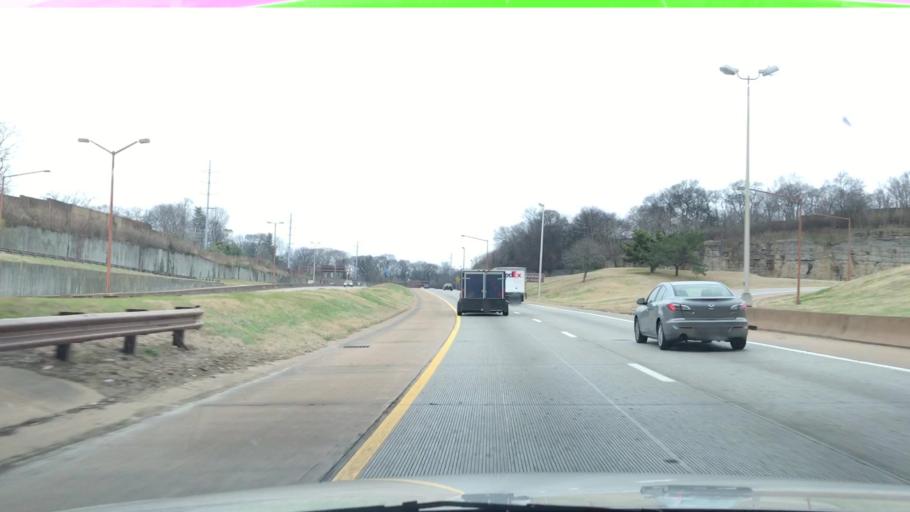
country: US
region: Tennessee
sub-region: Davidson County
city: Oak Hill
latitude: 36.1232
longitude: -86.8069
